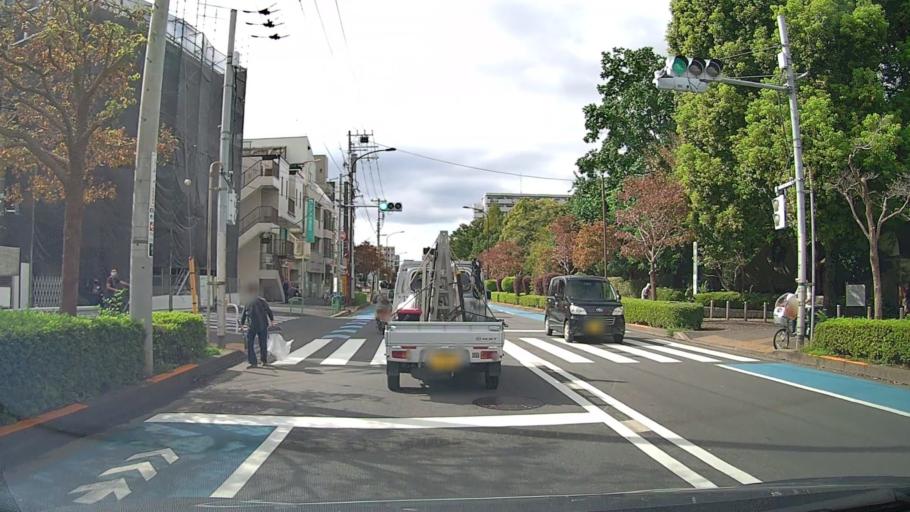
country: JP
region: Saitama
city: Wako
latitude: 35.7538
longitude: 139.6295
